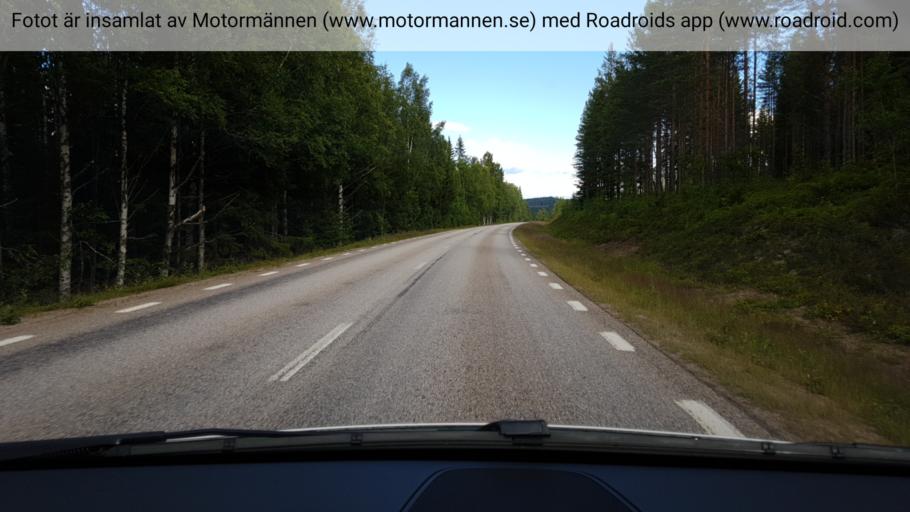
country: SE
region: Jaemtland
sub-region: Harjedalens Kommun
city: Sveg
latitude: 61.9797
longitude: 15.1057
